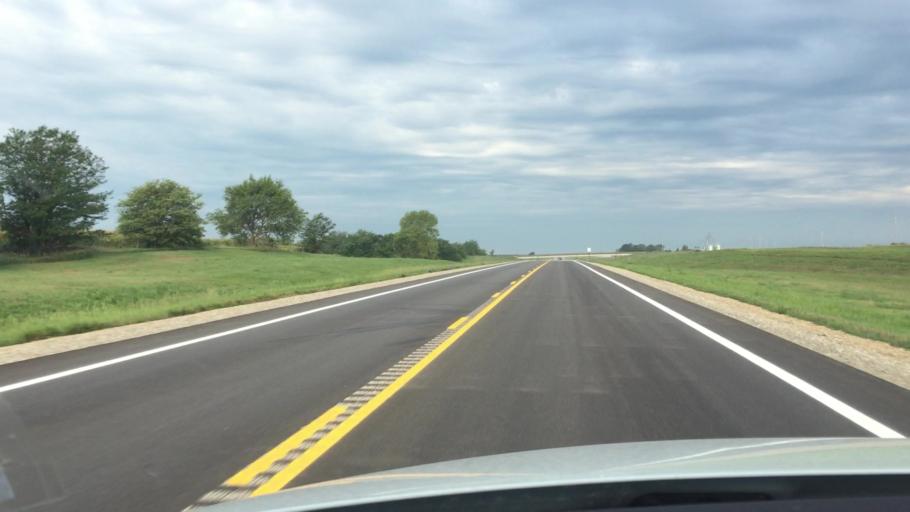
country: US
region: Kansas
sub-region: Doniphan County
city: Highland
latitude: 39.8412
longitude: -95.3890
